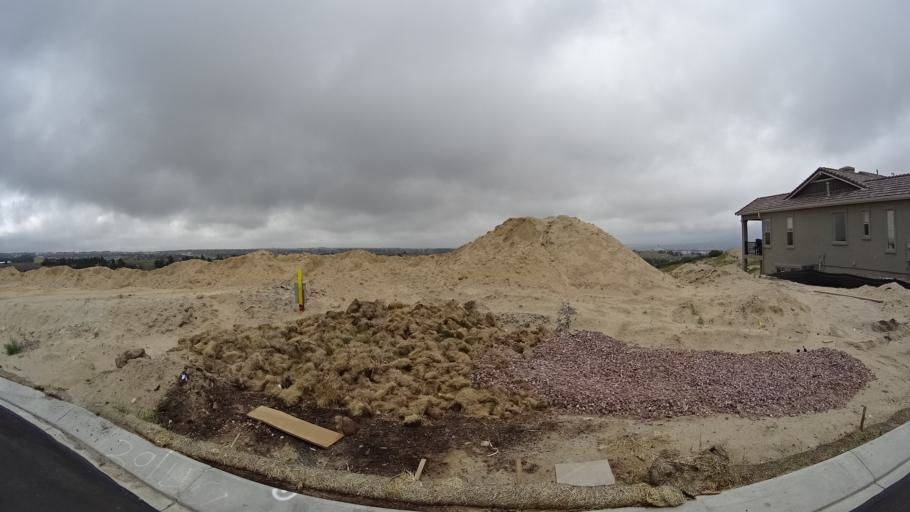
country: US
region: Colorado
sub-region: El Paso County
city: Gleneagle
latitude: 39.0070
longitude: -104.7847
